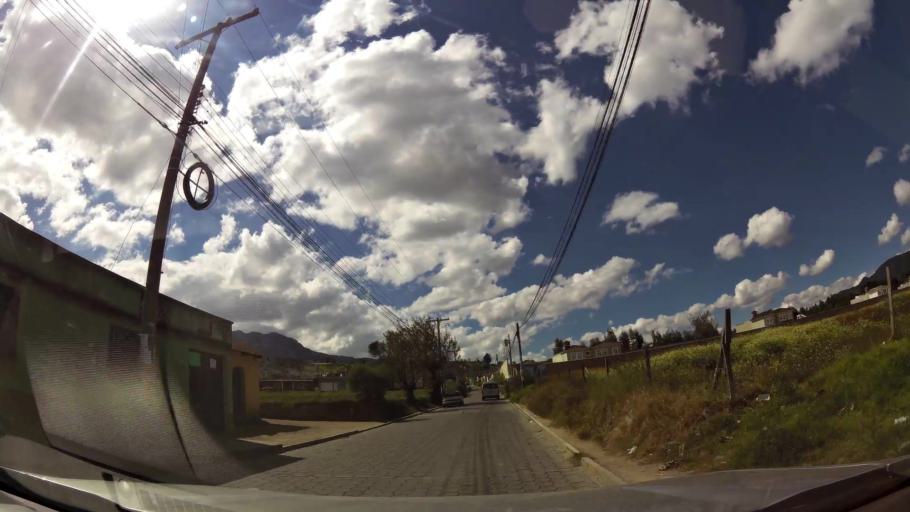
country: GT
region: Quetzaltenango
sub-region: Municipio de La Esperanza
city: La Esperanza
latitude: 14.8473
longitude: -91.5459
